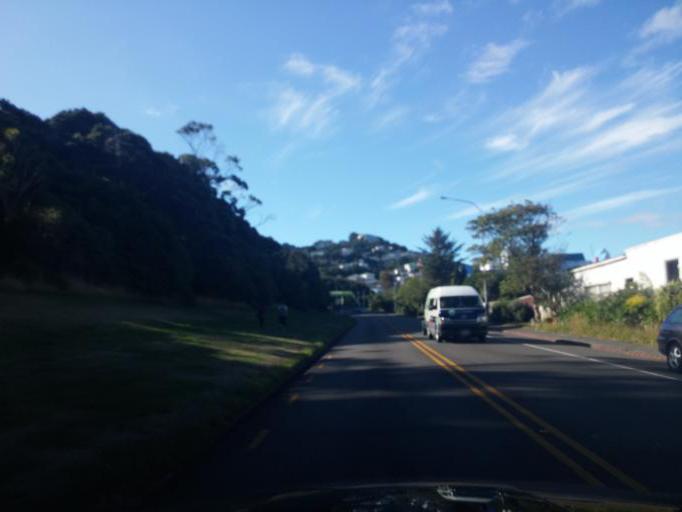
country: NZ
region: Wellington
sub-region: Wellington City
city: Wellington
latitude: -41.3071
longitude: 174.7921
